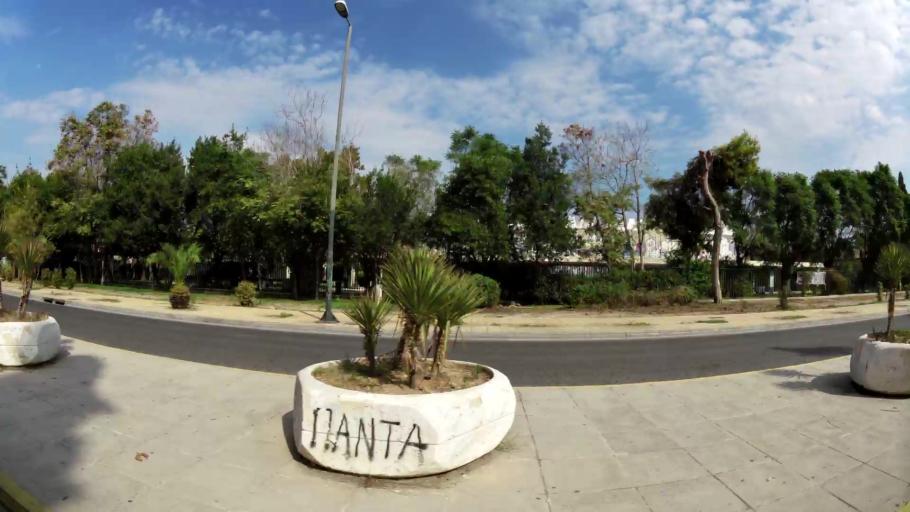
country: GR
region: Attica
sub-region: Nomarchia Athinas
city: Athens
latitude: 37.9829
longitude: 23.7063
